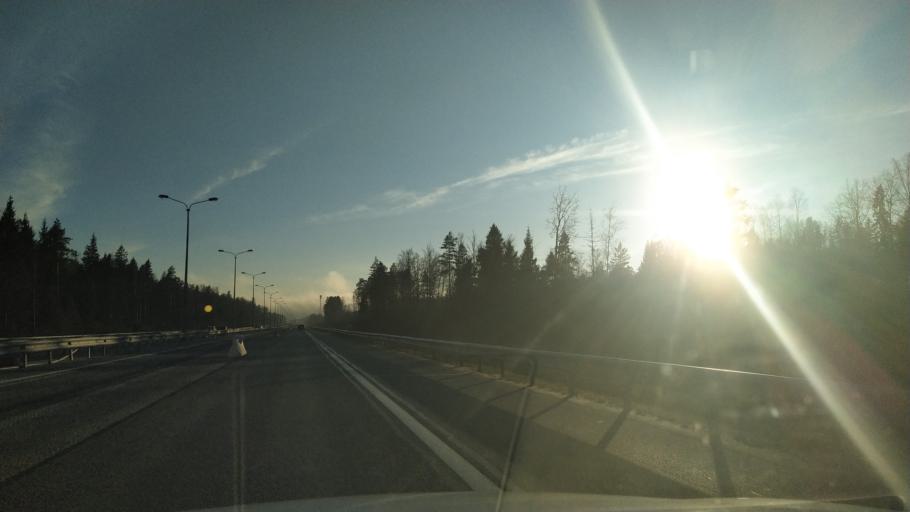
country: RU
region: St.-Petersburg
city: Ol'gino
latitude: 60.0508
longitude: 30.0832
